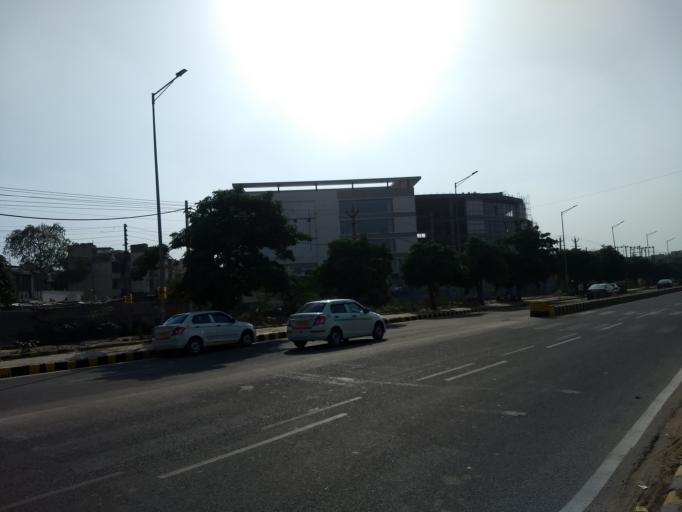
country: IN
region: Haryana
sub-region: Gurgaon
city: Gurgaon
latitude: 28.4349
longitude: 77.0699
